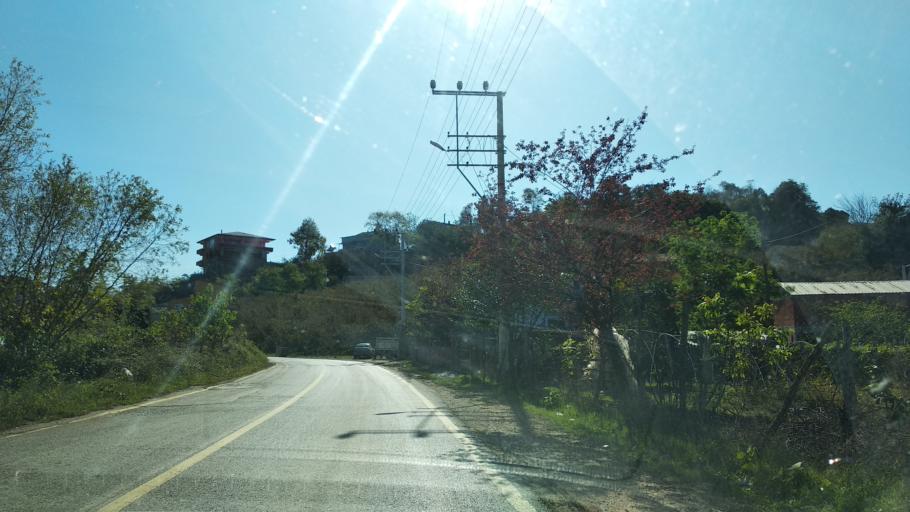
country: TR
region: Sakarya
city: Karasu
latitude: 41.1077
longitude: 30.6397
